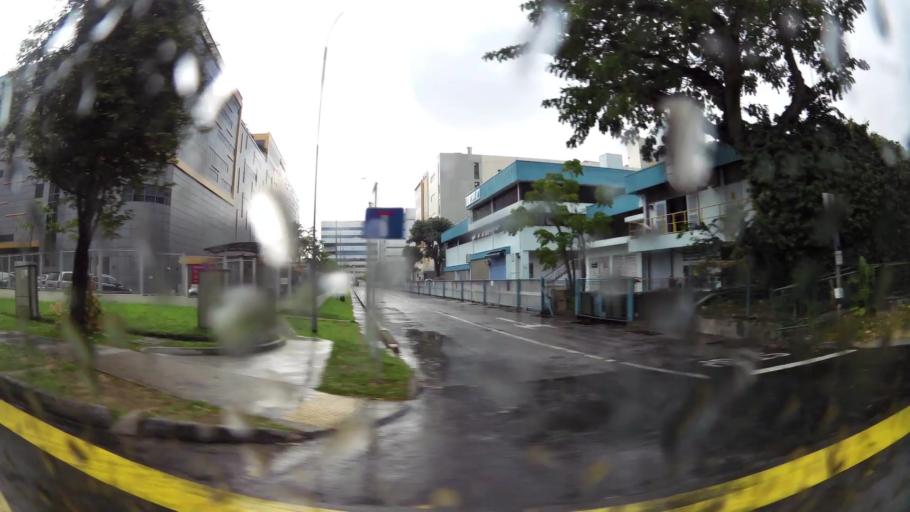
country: MY
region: Johor
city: Kampung Pasir Gudang Baru
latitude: 1.3908
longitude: 103.8487
